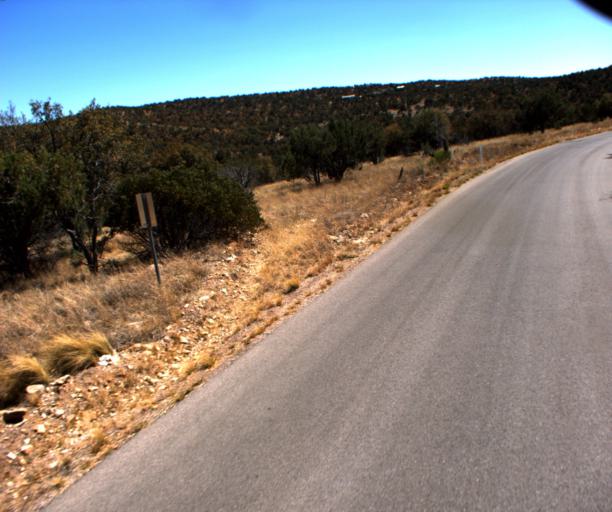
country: US
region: Arizona
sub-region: Cochise County
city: Sierra Vista
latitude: 31.4350
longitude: -110.4397
